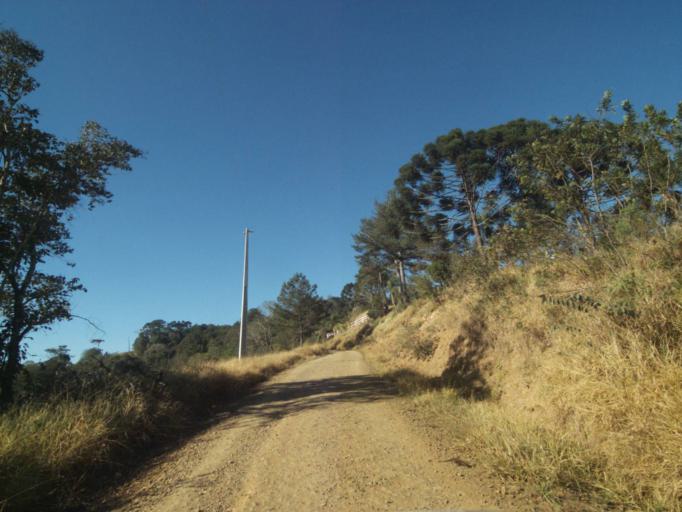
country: BR
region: Parana
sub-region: Tibagi
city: Tibagi
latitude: -24.5506
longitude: -50.5179
